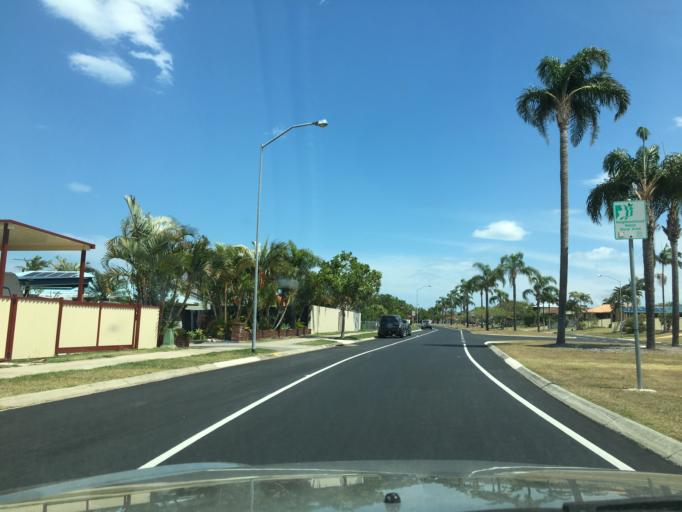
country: AU
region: Queensland
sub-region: Moreton Bay
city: Bongaree
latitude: -27.0791
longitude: 153.1367
